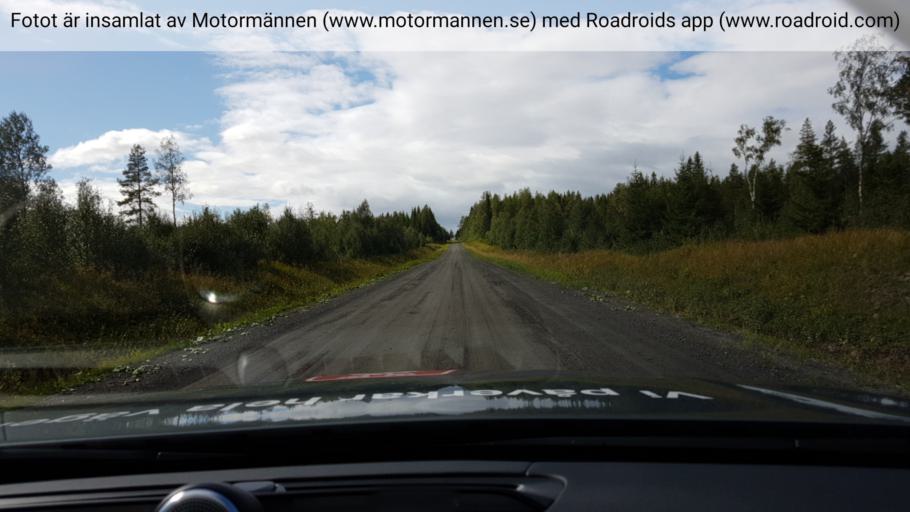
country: SE
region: Jaemtland
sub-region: OEstersunds Kommun
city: Lit
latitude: 63.6776
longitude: 14.7430
